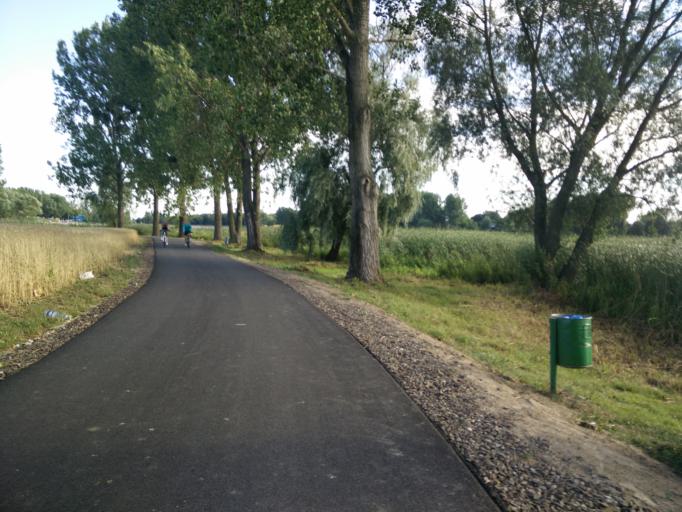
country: PL
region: Greater Poland Voivodeship
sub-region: Powiat sredzki
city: Sroda Wielkopolska
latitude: 52.2423
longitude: 17.2923
